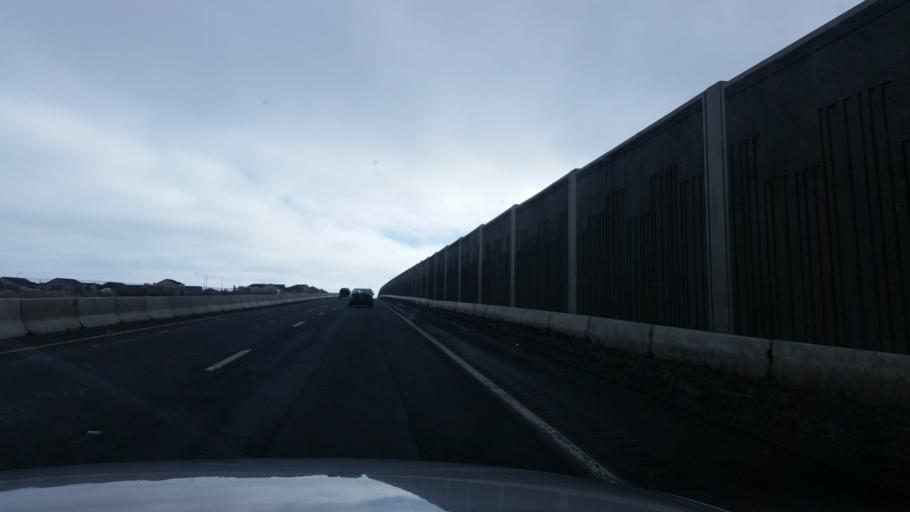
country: US
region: Washington
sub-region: Grant County
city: Moses Lake
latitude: 47.1296
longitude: -119.2570
